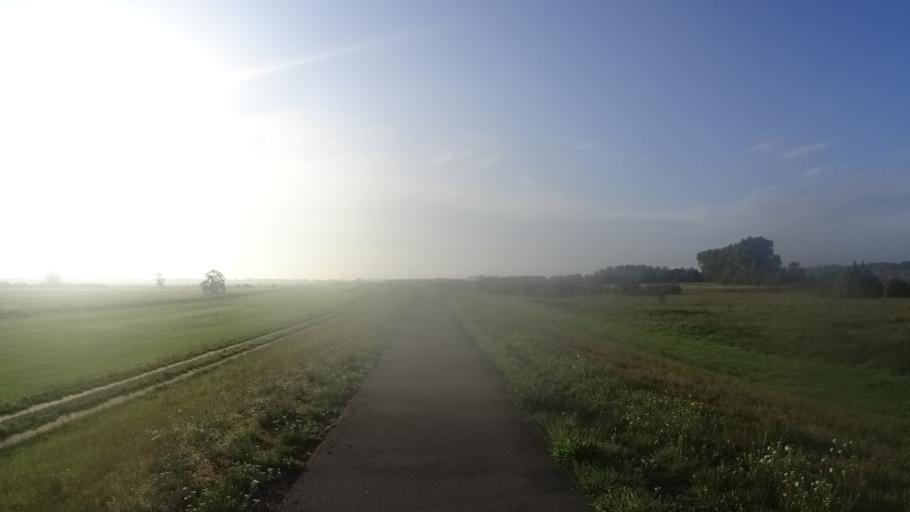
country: DE
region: Brandenburg
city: Lenzen
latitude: 53.0733
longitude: 11.4798
